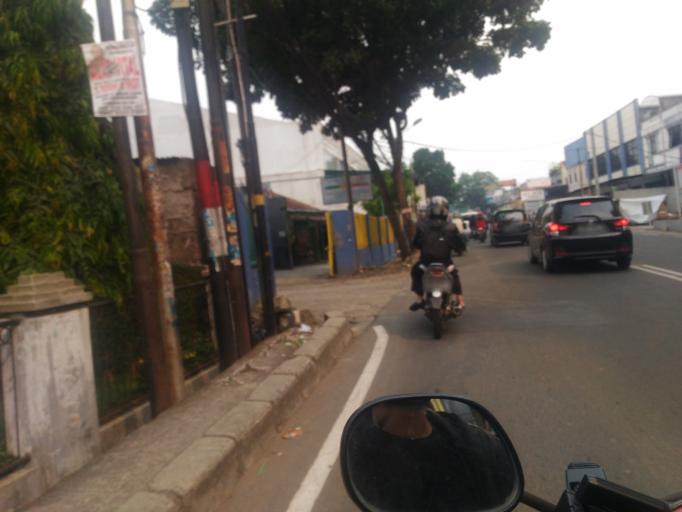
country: ID
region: West Java
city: Bogor
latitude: -6.6410
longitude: 106.8358
